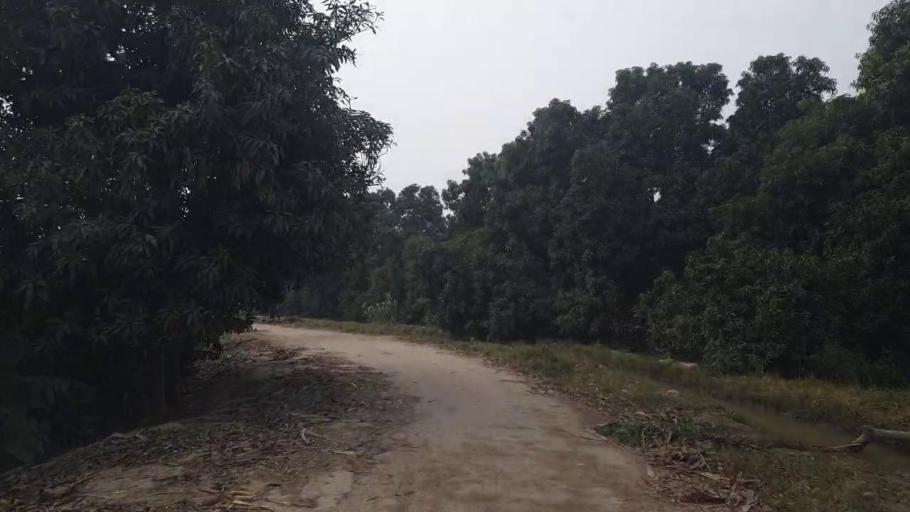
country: PK
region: Sindh
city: Tando Adam
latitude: 25.7141
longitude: 68.7006
